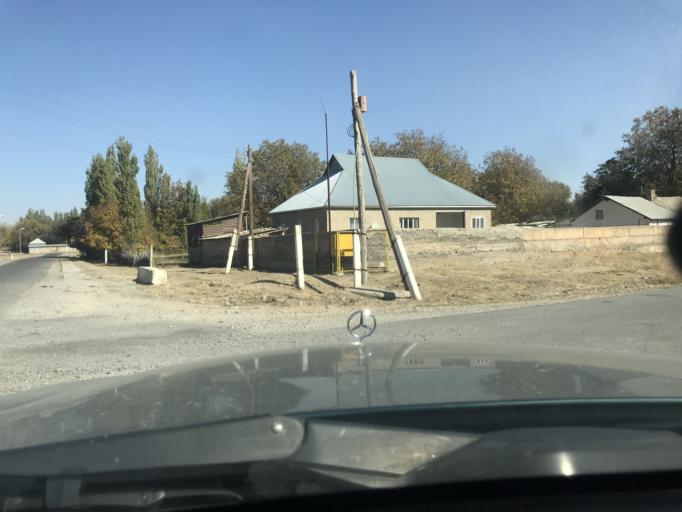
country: KZ
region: Ongtustik Qazaqstan
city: Sastobe
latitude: 42.5443
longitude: 69.9301
